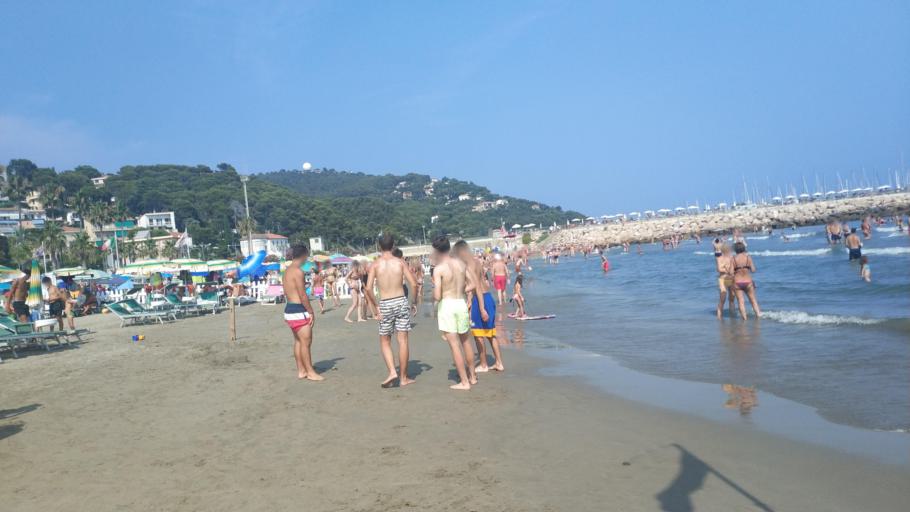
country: IT
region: Liguria
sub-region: Provincia di Savona
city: Marina di Andora
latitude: 43.9510
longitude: 8.1522
